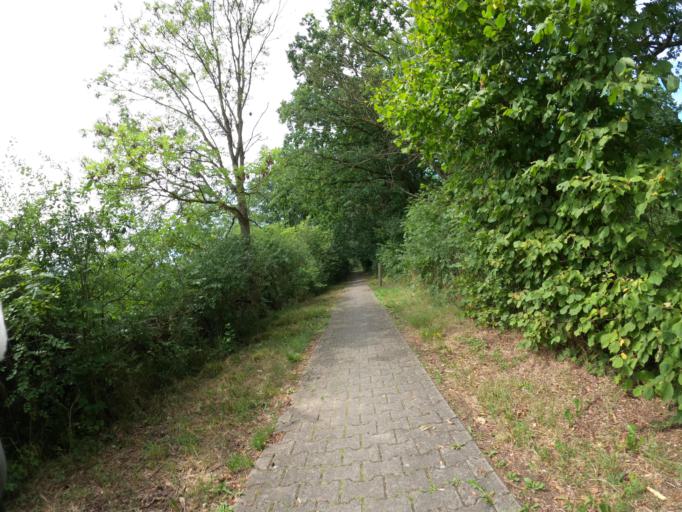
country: DE
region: Mecklenburg-Vorpommern
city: Woldegk
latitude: 53.4487
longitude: 13.5475
